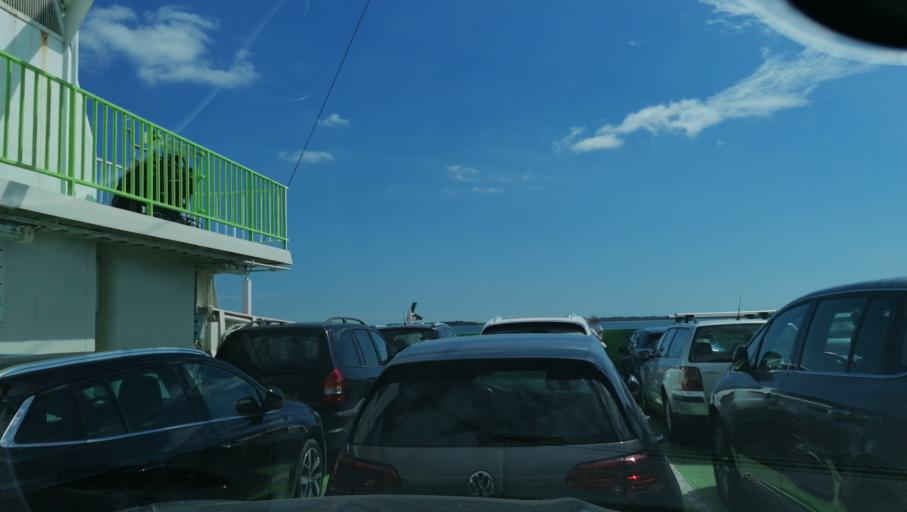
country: PT
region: Setubal
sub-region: Setubal
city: Setubal
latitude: 38.5139
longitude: -8.8856
